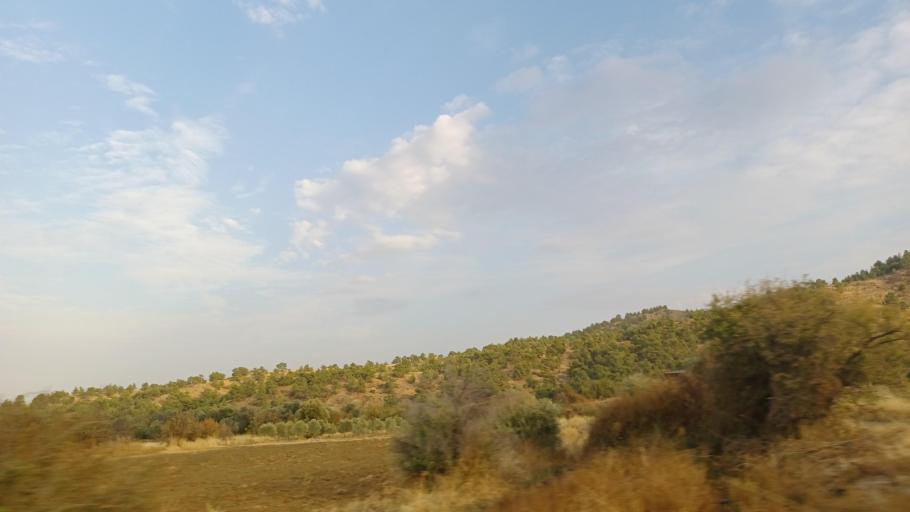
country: CY
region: Lefkosia
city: Kakopetria
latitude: 35.0632
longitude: 32.9154
